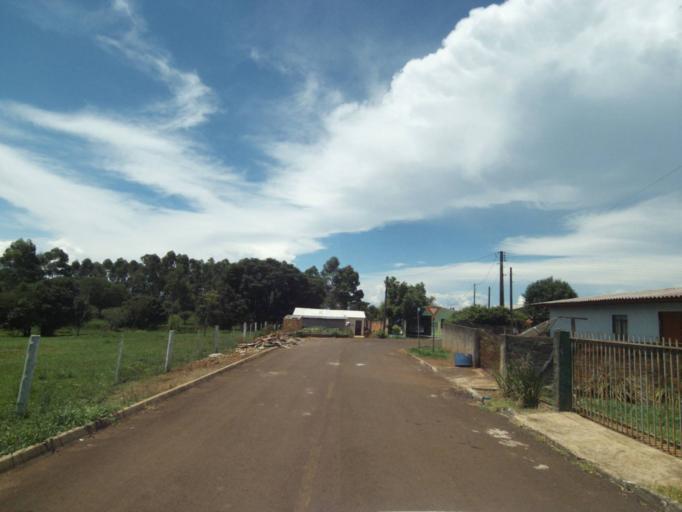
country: BR
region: Parana
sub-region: Guaraniacu
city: Guaraniacu
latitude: -25.0892
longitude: -52.8769
